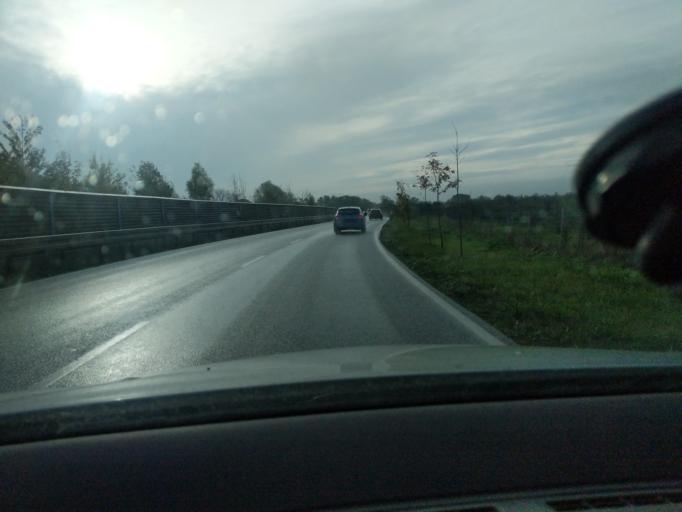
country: DE
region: Lower Saxony
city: Neu Wulmstorf
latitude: 53.5249
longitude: 9.8250
